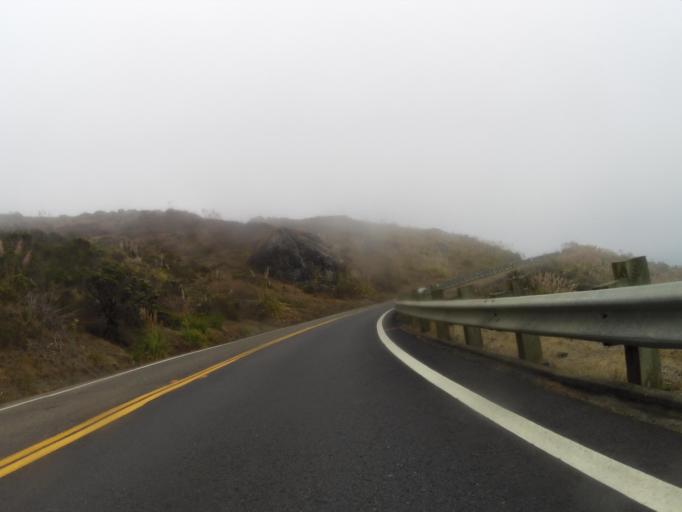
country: US
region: California
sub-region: Sonoma County
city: Monte Rio
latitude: 38.4813
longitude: -123.1699
